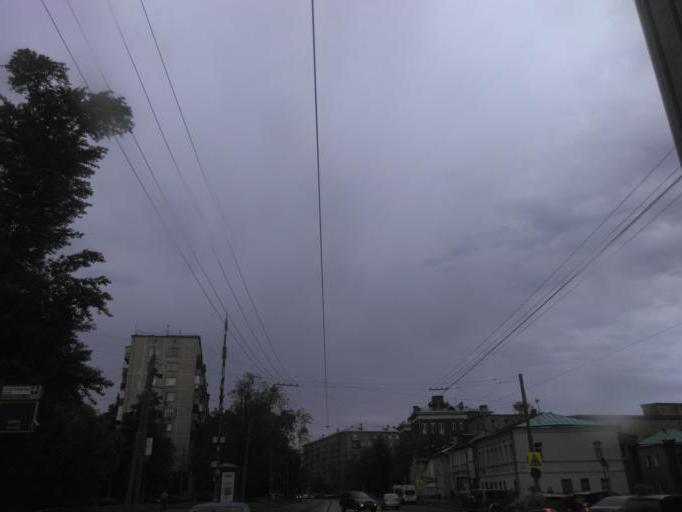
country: RU
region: Moscow
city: Zamoskvorech'ye
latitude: 55.7249
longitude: 37.6368
